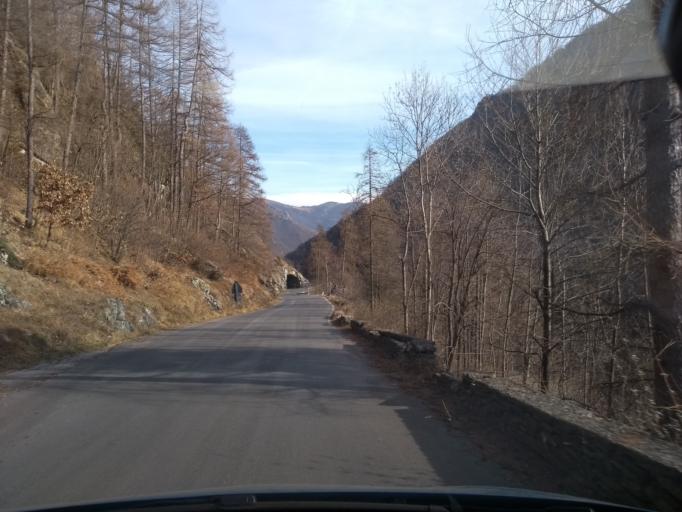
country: IT
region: Piedmont
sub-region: Provincia di Torino
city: Ala di Stura
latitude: 45.3140
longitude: 7.3264
